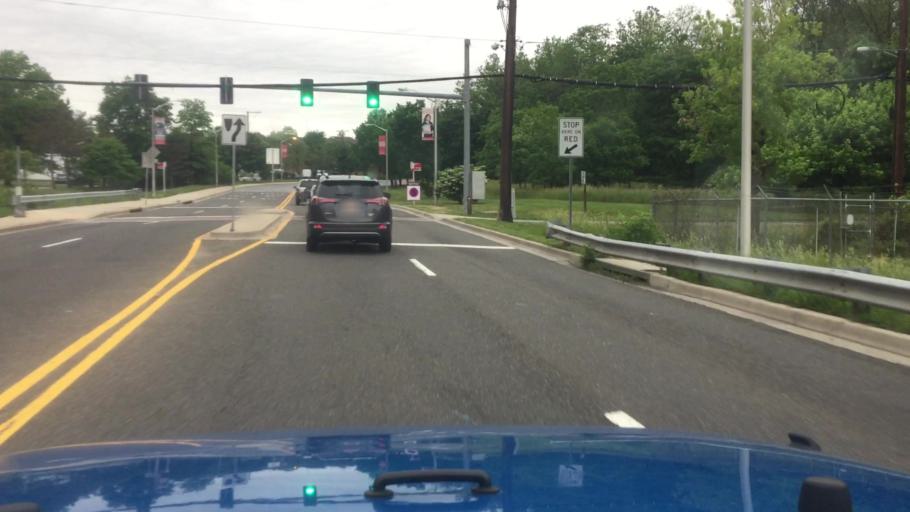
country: US
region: Maryland
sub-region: Prince George's County
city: College Park
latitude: 38.9834
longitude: -76.9305
